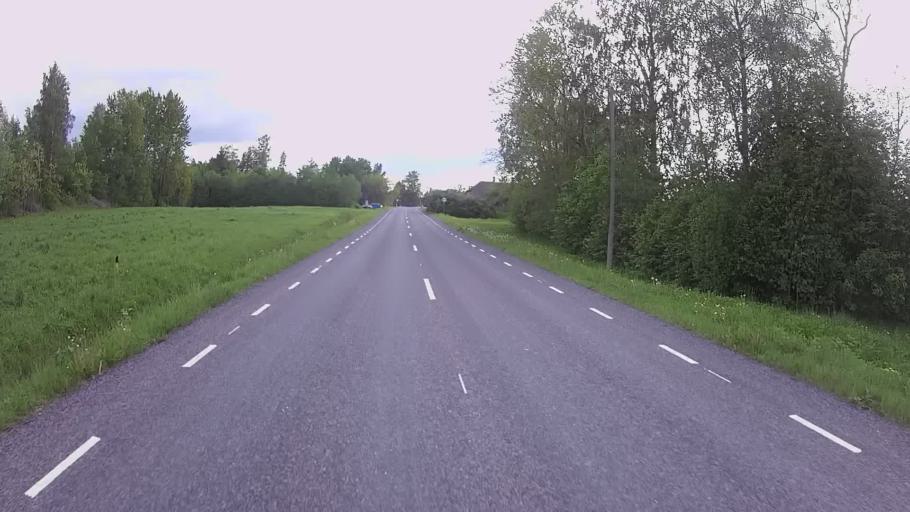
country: EE
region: Jogevamaa
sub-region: Mustvee linn
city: Mustvee
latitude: 58.9975
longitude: 26.8973
